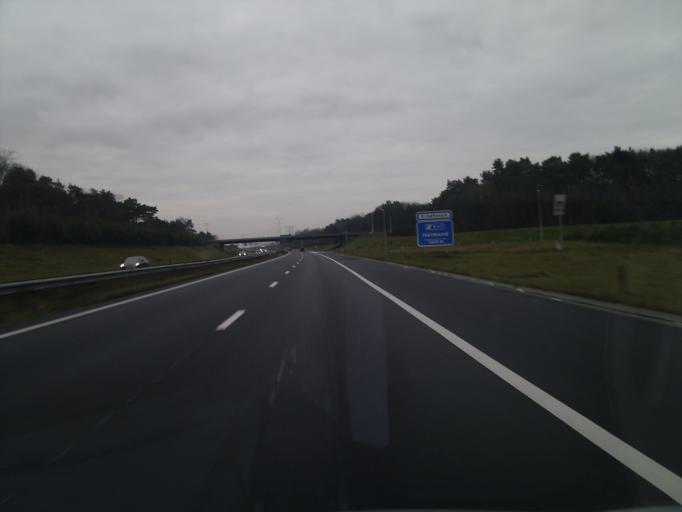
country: NL
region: North Brabant
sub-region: Gemeente Son en Breugel
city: Son
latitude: 51.5158
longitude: 5.4686
